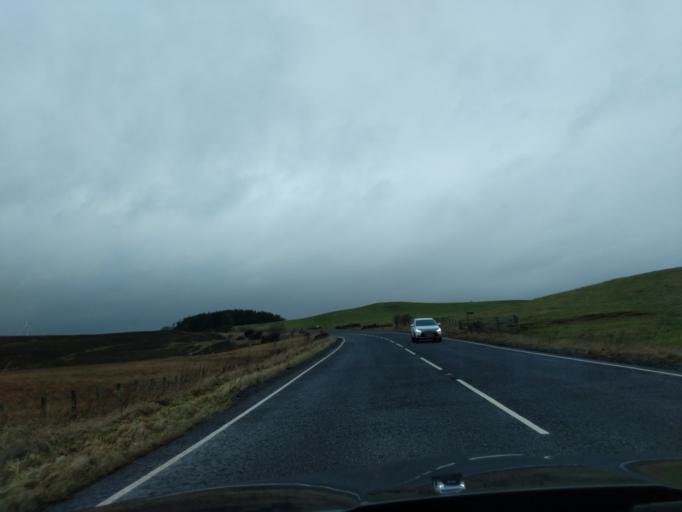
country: GB
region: England
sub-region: Northumberland
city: Rothley
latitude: 55.1732
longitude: -2.0261
